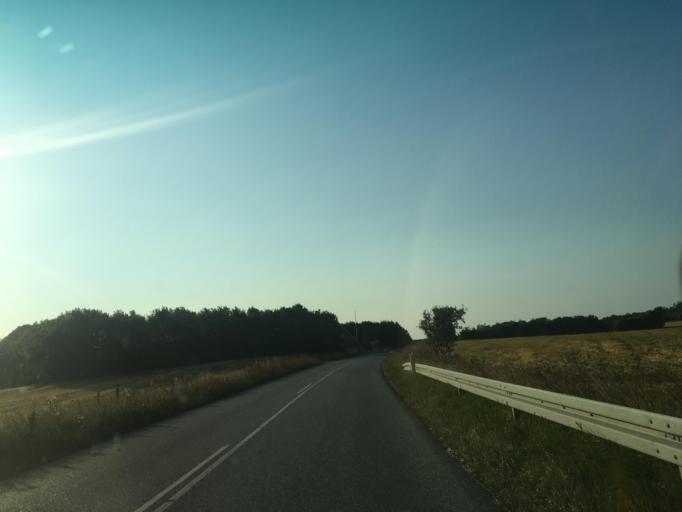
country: DK
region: North Denmark
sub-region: Thisted Kommune
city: Hurup
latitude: 56.7812
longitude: 8.4186
